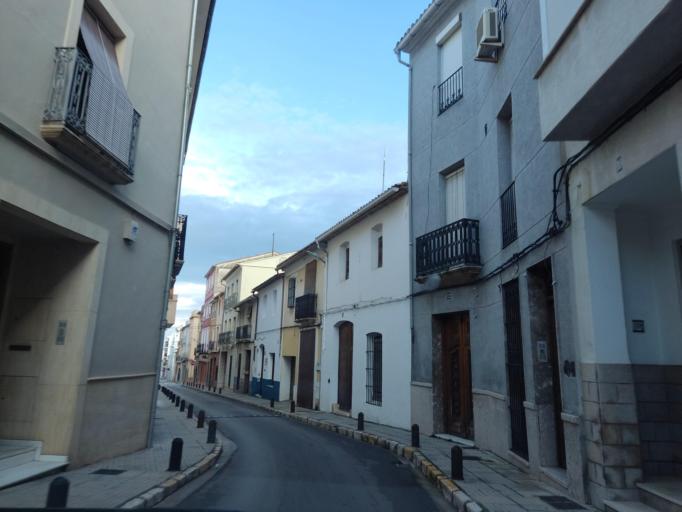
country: ES
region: Valencia
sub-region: Provincia de Alicante
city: Pego
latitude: 38.8397
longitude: -0.1168
